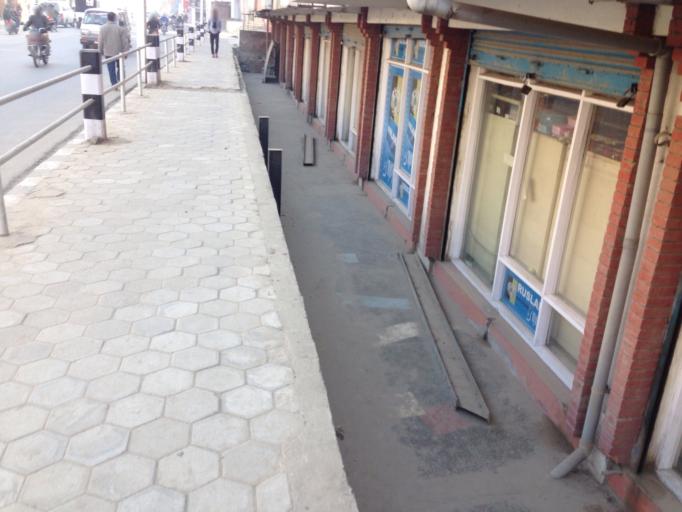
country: NP
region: Central Region
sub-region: Bagmati Zone
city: Kathmandu
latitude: 27.7208
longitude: 85.3195
